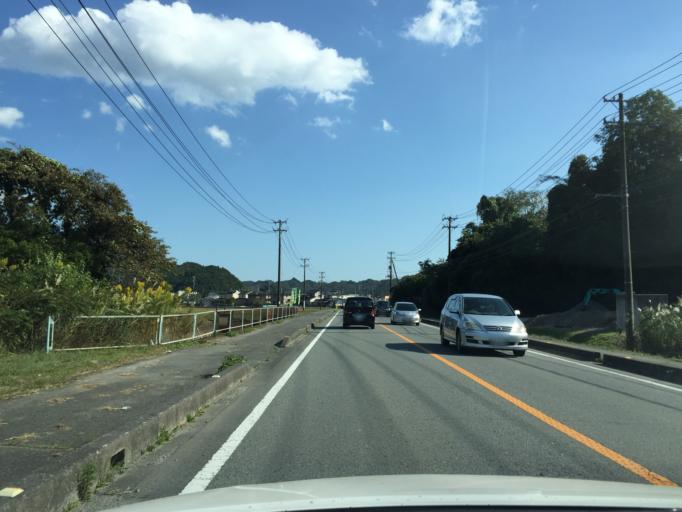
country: JP
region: Fukushima
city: Iwaki
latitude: 36.9990
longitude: 140.9015
